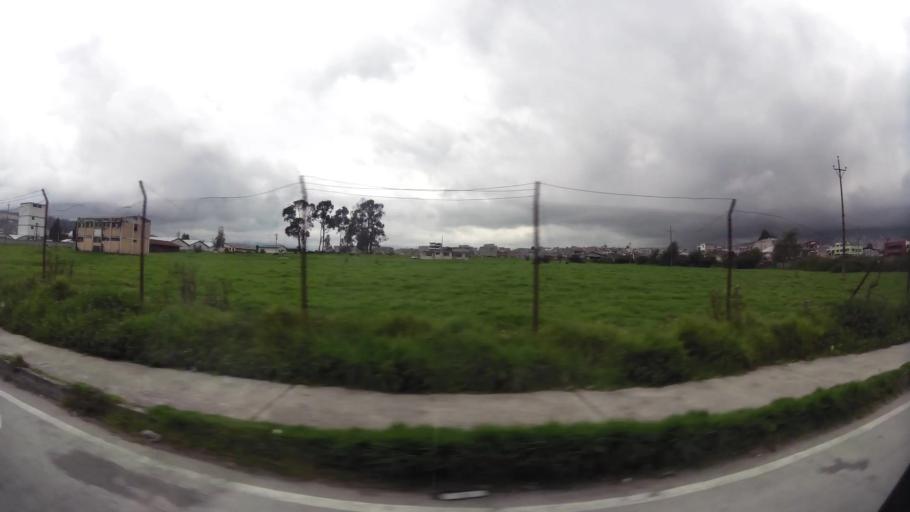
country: EC
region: Pichincha
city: Quito
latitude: -0.3181
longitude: -78.5444
